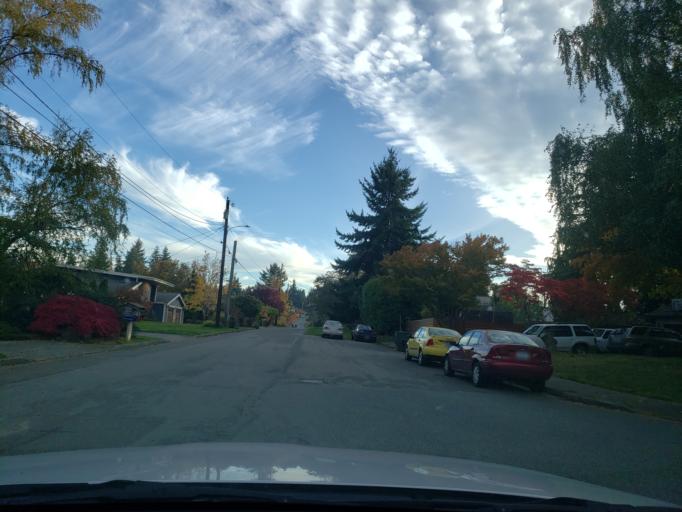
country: US
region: Washington
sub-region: Snohomish County
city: Edmonds
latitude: 47.8178
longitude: -122.3644
